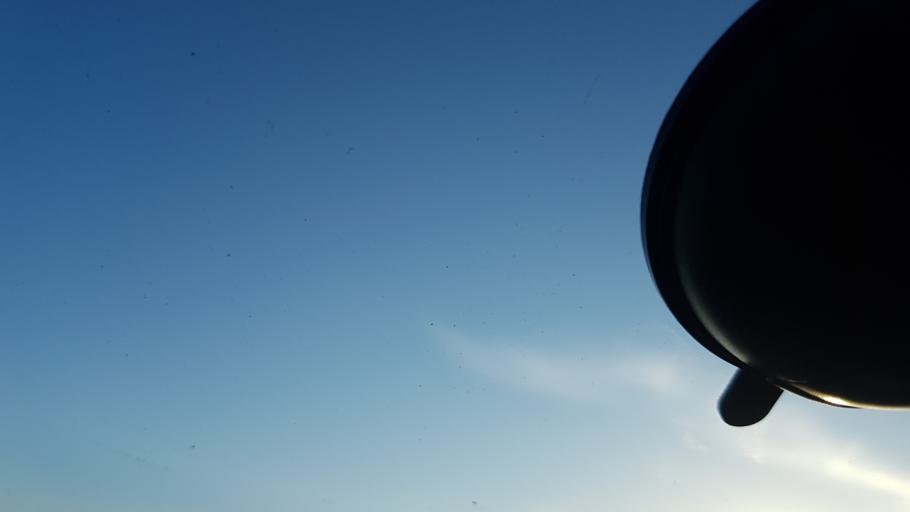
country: PL
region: Masovian Voivodeship
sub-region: Warszawa
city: Wawer
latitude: 52.1682
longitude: 21.2058
